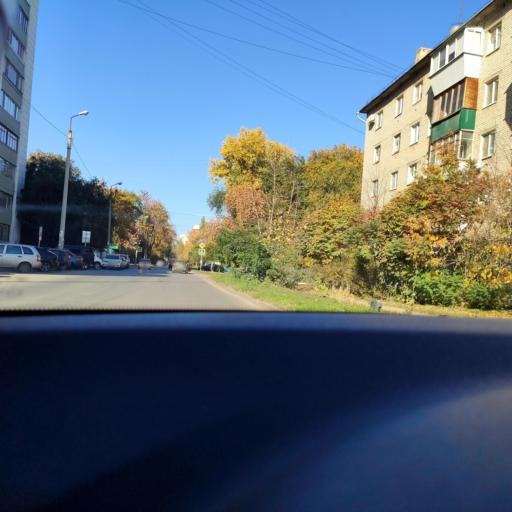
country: RU
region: Samara
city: Petra-Dubrava
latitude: 53.2280
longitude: 50.2757
